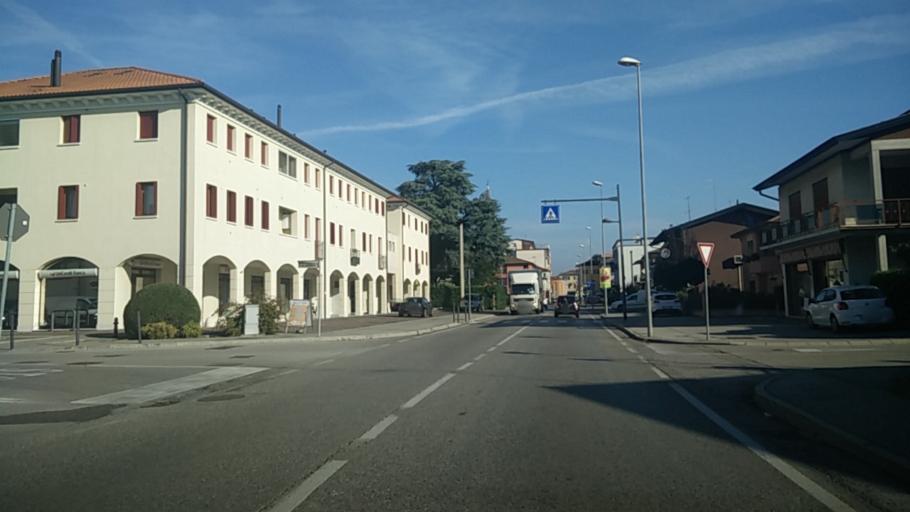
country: IT
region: Veneto
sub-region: Provincia di Padova
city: Trebaseleghe
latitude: 45.5882
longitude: 12.0512
